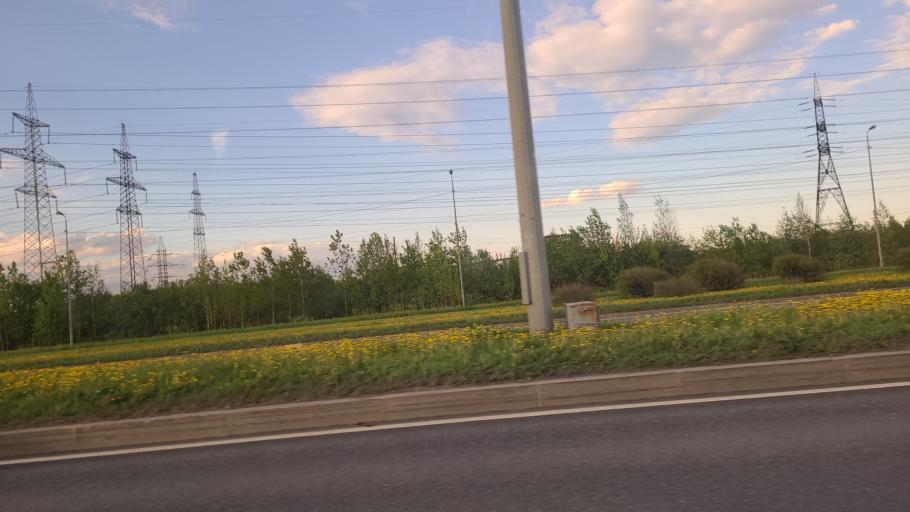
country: RU
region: St.-Petersburg
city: Petro-Slavyanka
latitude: 59.7564
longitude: 30.5183
